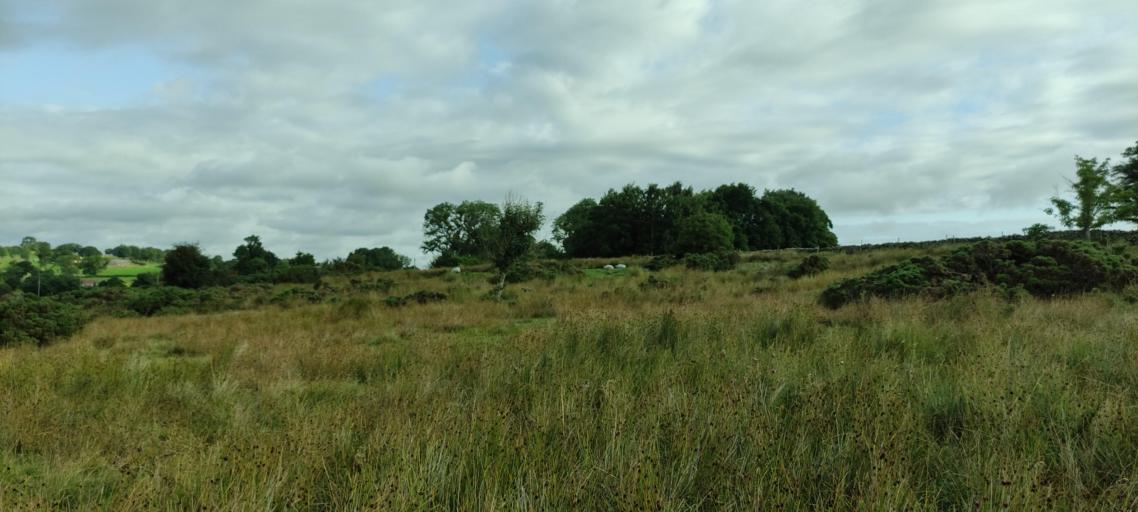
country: GB
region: England
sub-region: Cumbria
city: Keswick
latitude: 54.7073
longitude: -2.9975
